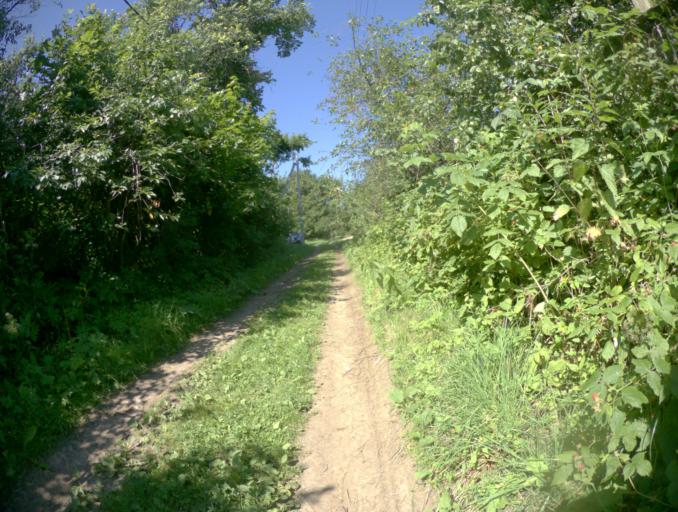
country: RU
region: Nizjnij Novgorod
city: Reshetikha
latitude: 56.1659
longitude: 43.3479
